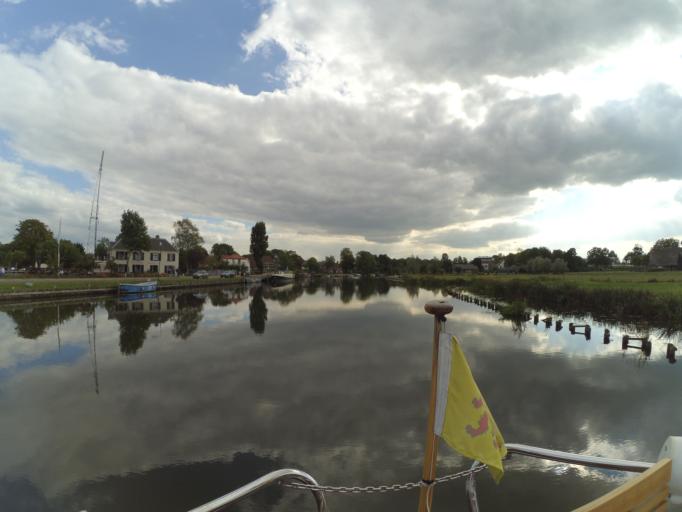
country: NL
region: Utrecht
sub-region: Stichtse Vecht
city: Maarssen
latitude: 52.1521
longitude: 5.0347
